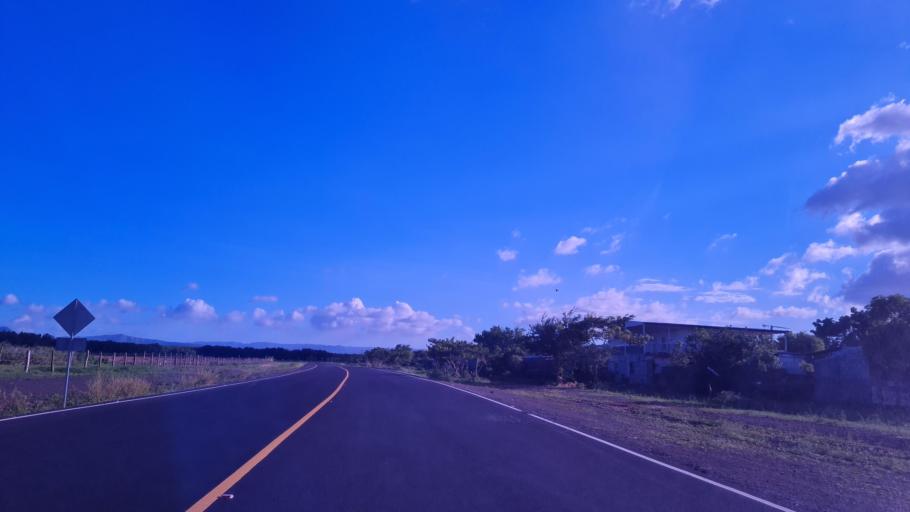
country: NI
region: Masaya
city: Ticuantepe
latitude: 12.1036
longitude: -86.1570
